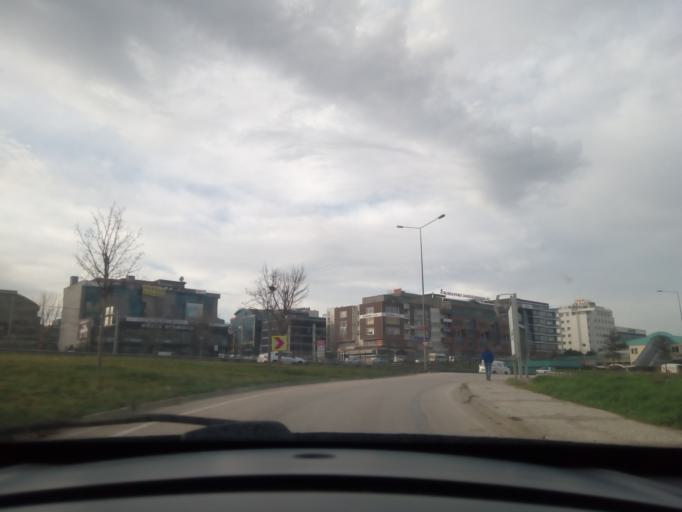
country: TR
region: Bursa
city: Cali
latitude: 40.2132
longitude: 28.9517
